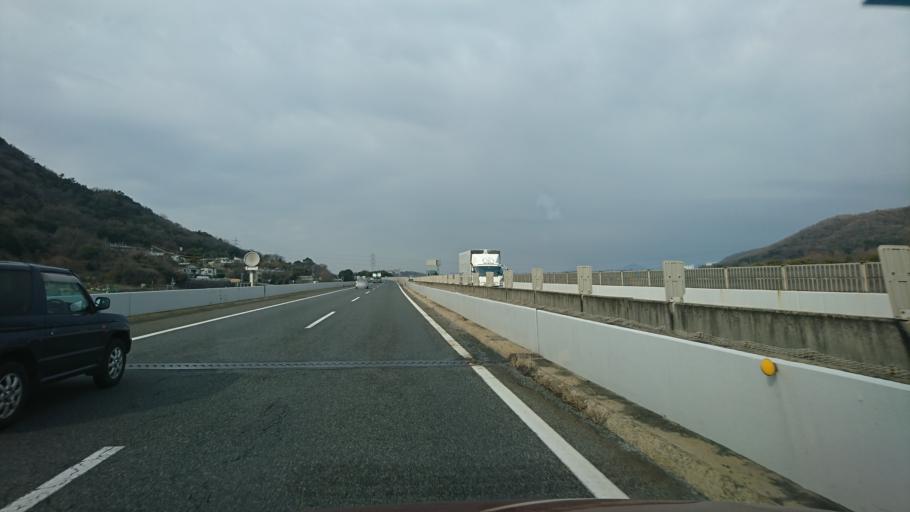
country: JP
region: Hiroshima
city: Fukuyama
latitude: 34.5147
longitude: 133.3917
